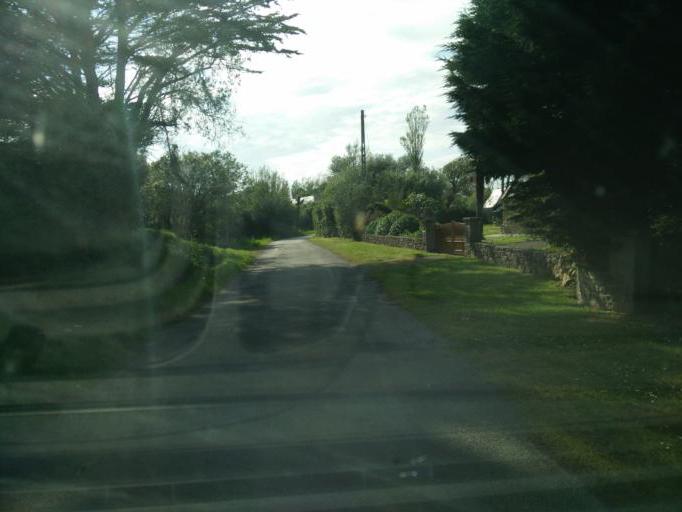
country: FR
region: Brittany
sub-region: Departement du Finistere
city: Crozon
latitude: 48.2342
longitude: -4.5458
